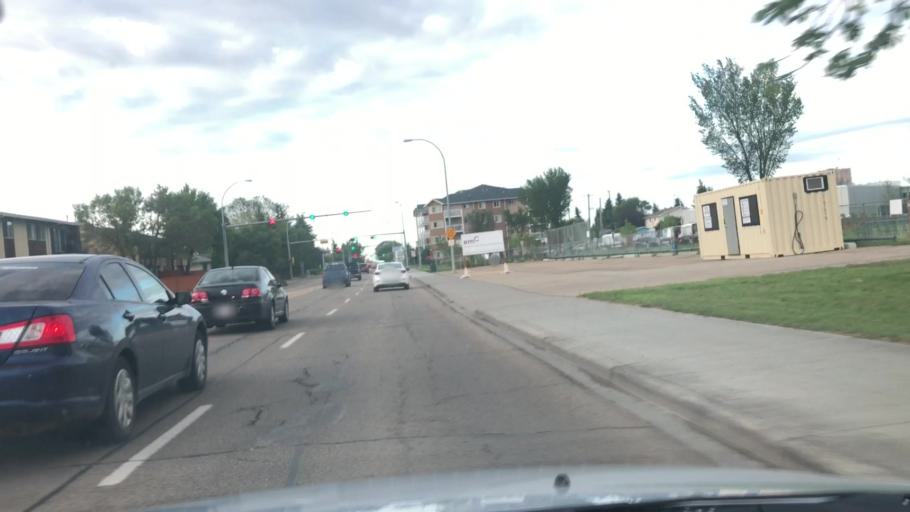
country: CA
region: Alberta
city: Edmonton
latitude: 53.5914
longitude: -113.5413
